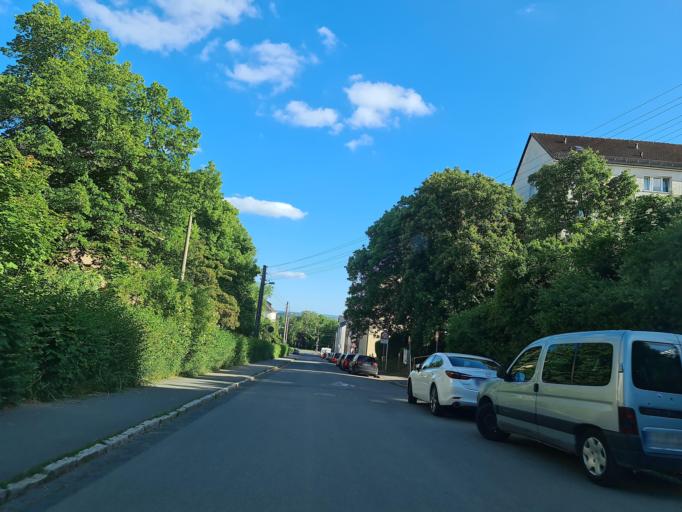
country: DE
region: Saxony
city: Plauen
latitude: 50.4950
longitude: 12.0899
